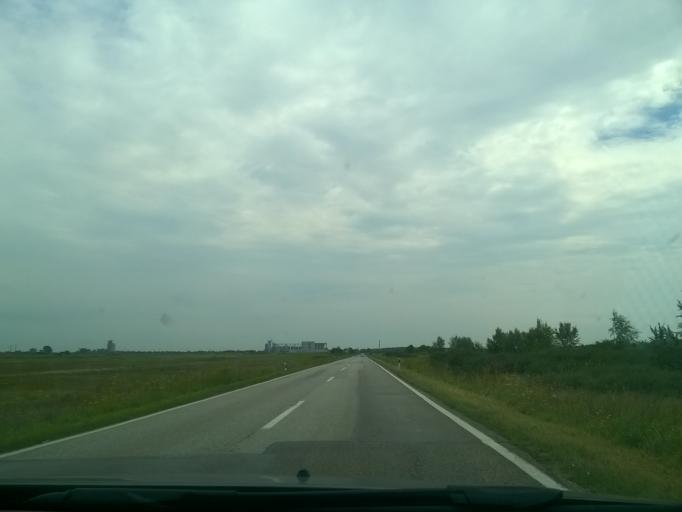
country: RS
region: Autonomna Pokrajina Vojvodina
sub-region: Srednjebanatski Okrug
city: Secanj
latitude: 45.3730
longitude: 20.7457
